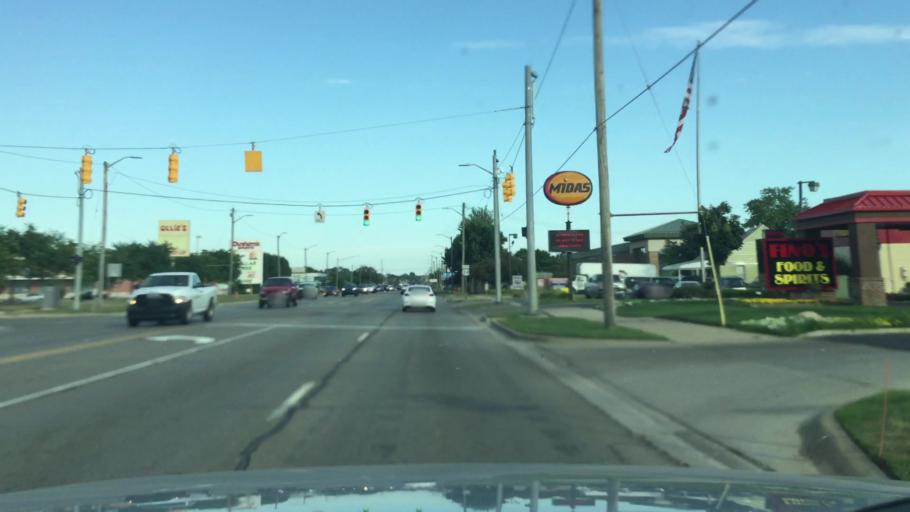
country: US
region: Michigan
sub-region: Oakland County
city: Waterford
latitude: 42.6934
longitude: -83.3907
